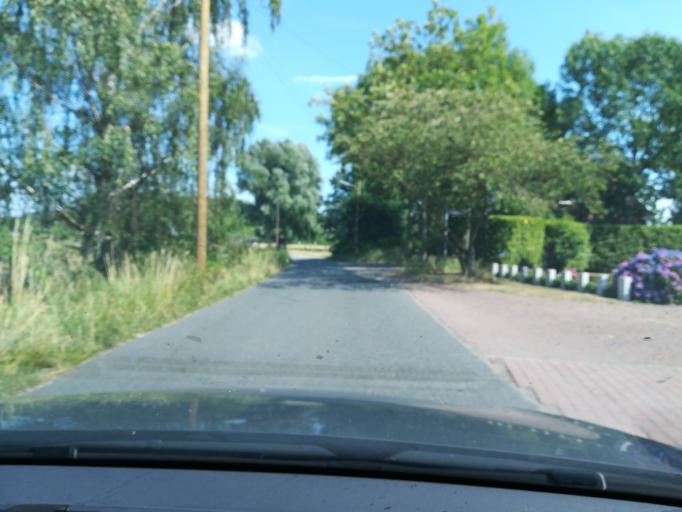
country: DE
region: Hamburg
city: Rothenburgsort
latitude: 53.4938
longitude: 10.0253
